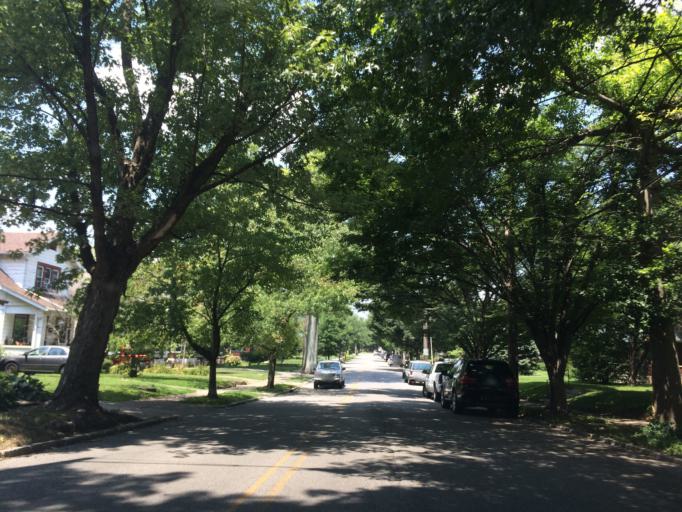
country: US
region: Kentucky
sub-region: Jefferson County
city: Indian Hills
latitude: 38.2584
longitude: -85.6848
